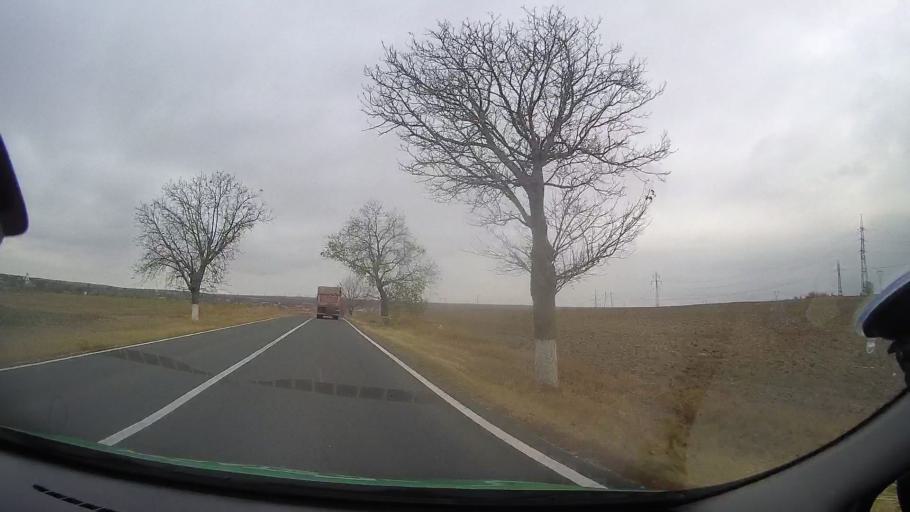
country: RO
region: Constanta
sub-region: Comuna Castelu
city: Castelu
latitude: 44.2566
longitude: 28.3502
